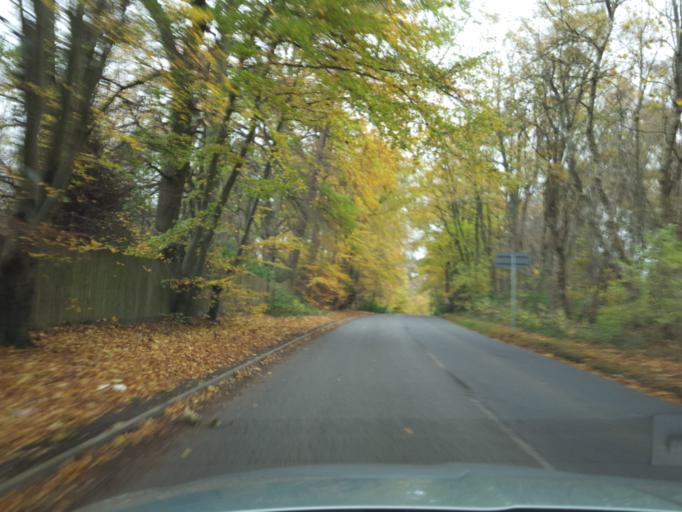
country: GB
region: Scotland
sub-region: Midlothian
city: Penicuik
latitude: 55.8432
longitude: -3.2234
